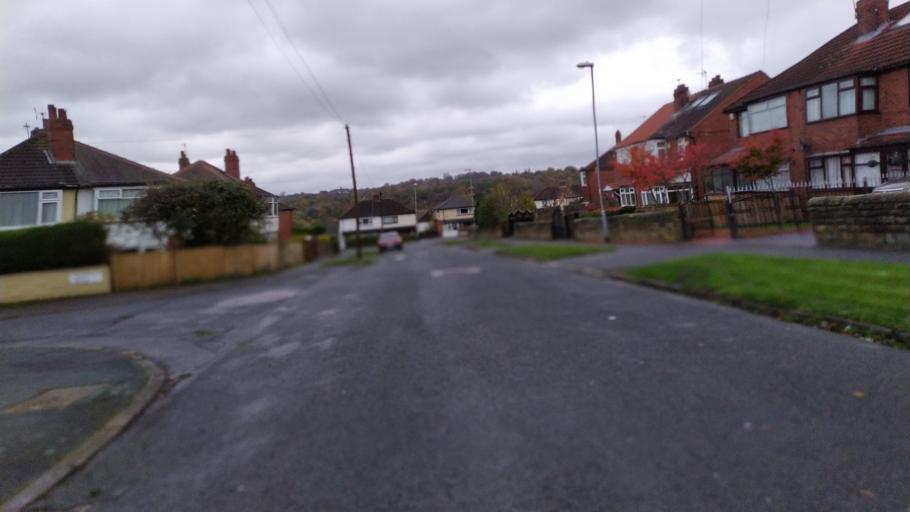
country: GB
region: England
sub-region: City and Borough of Leeds
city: Leeds
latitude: 53.8119
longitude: -1.5905
